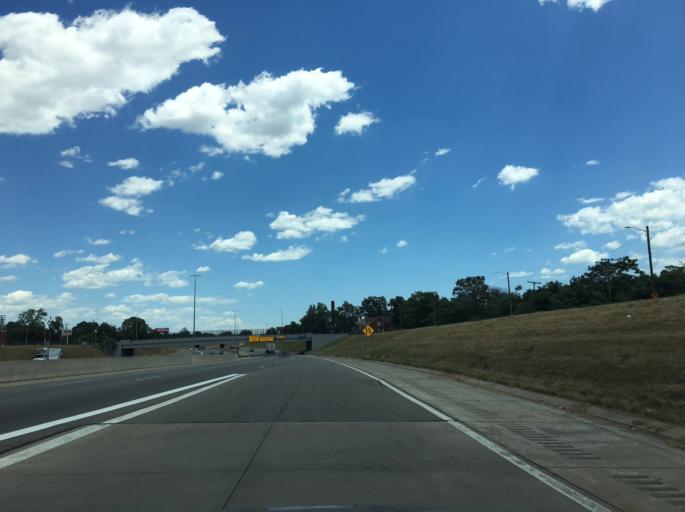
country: US
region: Michigan
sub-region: Wayne County
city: Highland Park
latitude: 42.4098
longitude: -83.0750
